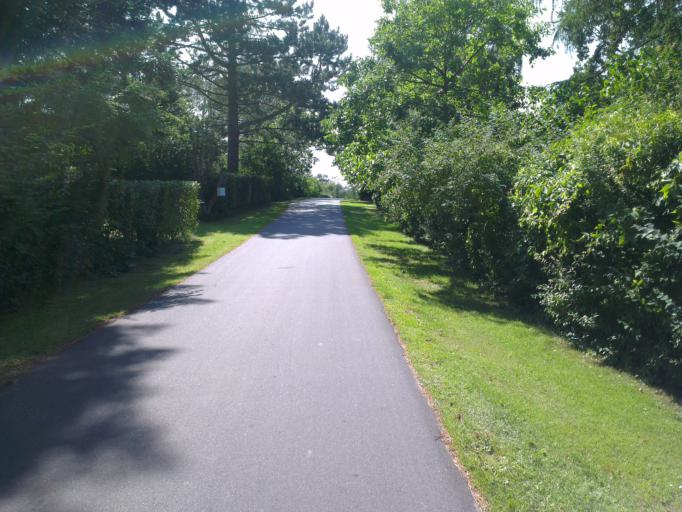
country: DK
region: Capital Region
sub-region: Halsnaes Kommune
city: Hundested
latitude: 55.9193
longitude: 11.9156
